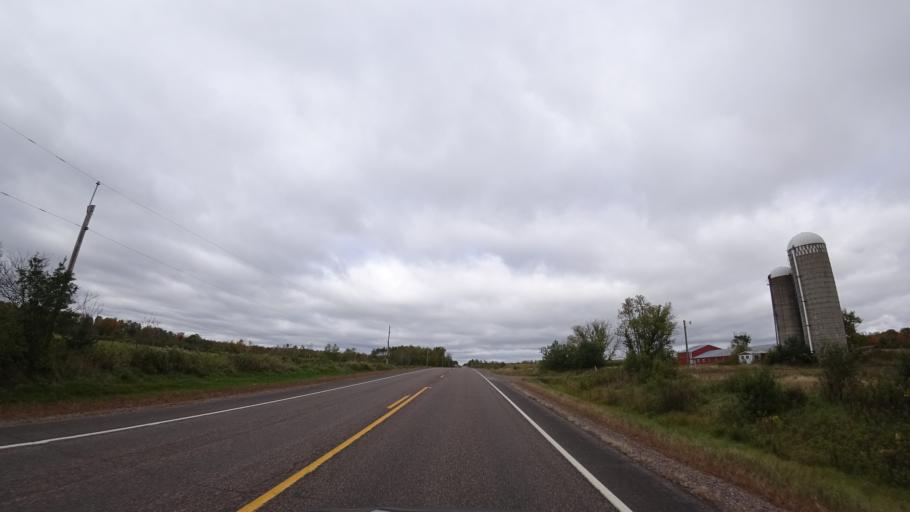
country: US
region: Wisconsin
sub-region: Rusk County
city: Ladysmith
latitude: 45.3945
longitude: -91.1102
